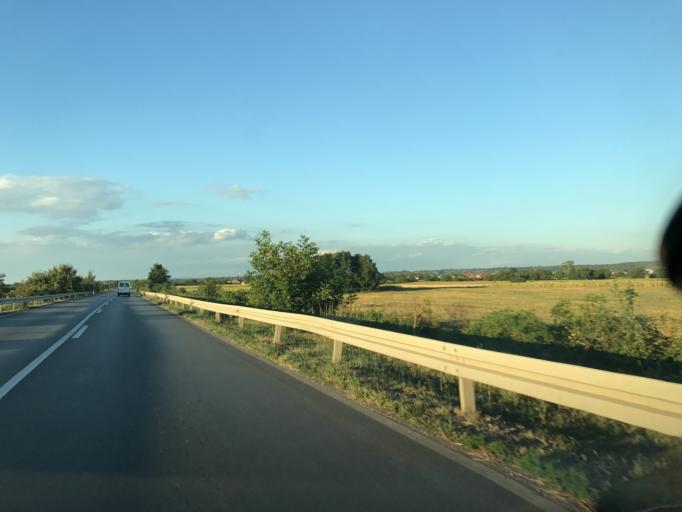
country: RS
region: Central Serbia
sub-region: Branicevski Okrug
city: Pozarevac
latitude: 44.6379
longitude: 21.1499
